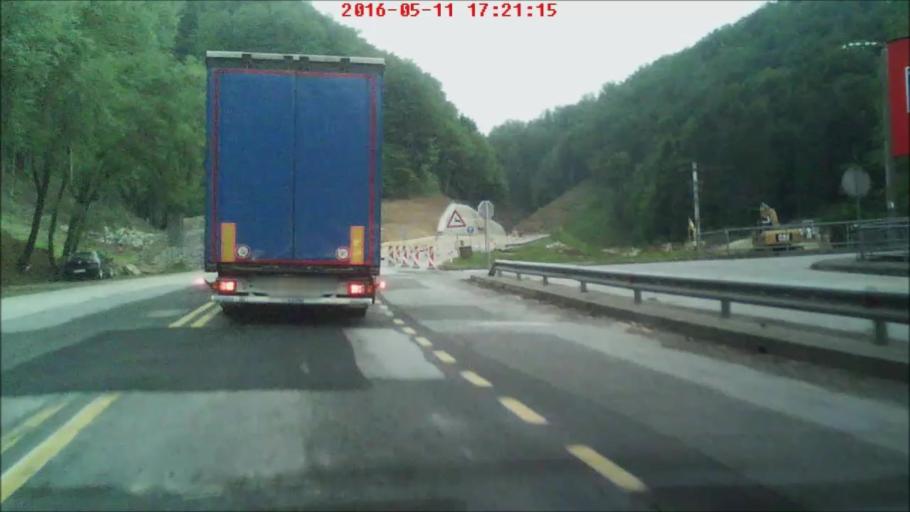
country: SI
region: Zetale
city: Zetale
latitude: 46.2866
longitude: 15.8589
